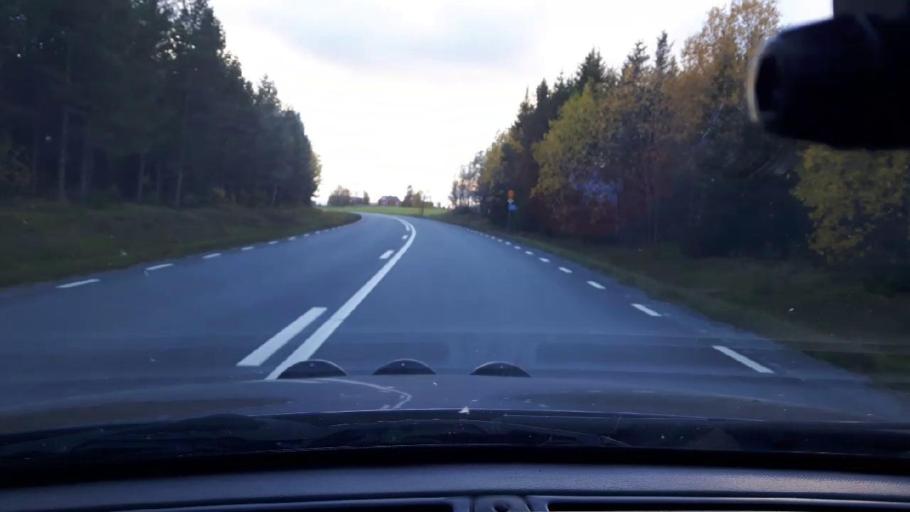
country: SE
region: Jaemtland
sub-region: Krokoms Kommun
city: Krokom
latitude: 63.0810
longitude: 14.2918
